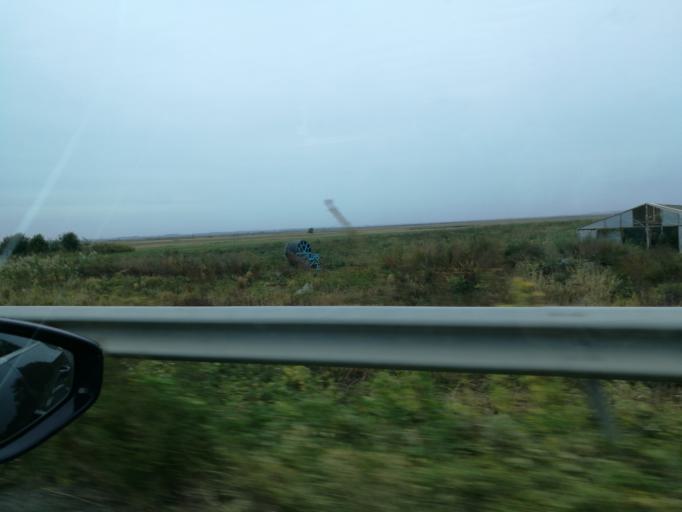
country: RO
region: Tulcea
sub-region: Oras Macin
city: Macin
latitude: 45.2591
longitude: 28.0800
